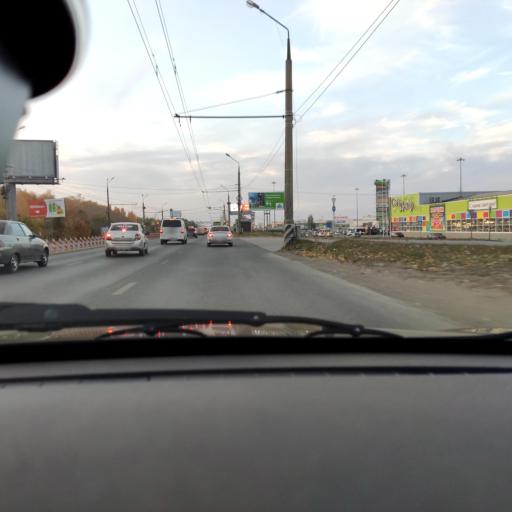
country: RU
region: Samara
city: Tol'yatti
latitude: 53.5385
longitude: 49.3912
